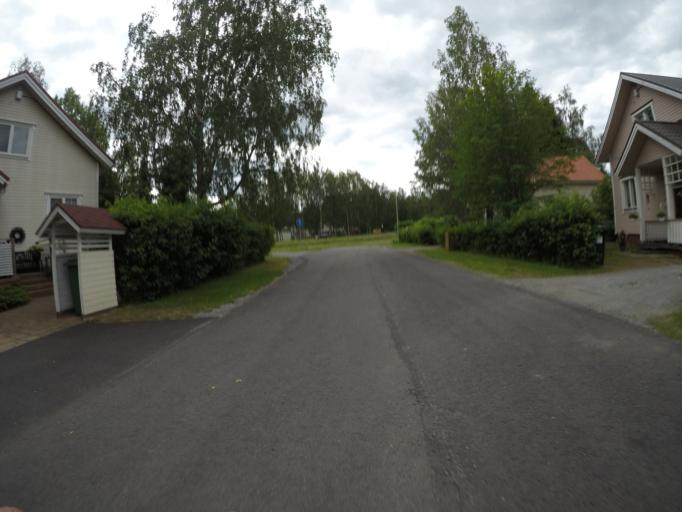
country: FI
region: Haeme
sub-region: Haemeenlinna
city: Haemeenlinna
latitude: 60.9895
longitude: 24.4315
